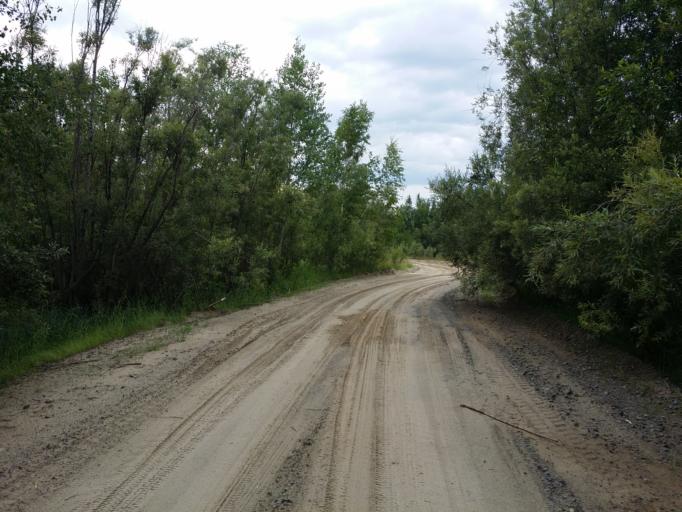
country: RU
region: Khanty-Mansiyskiy Avtonomnyy Okrug
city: Megion
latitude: 60.9461
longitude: 76.3001
